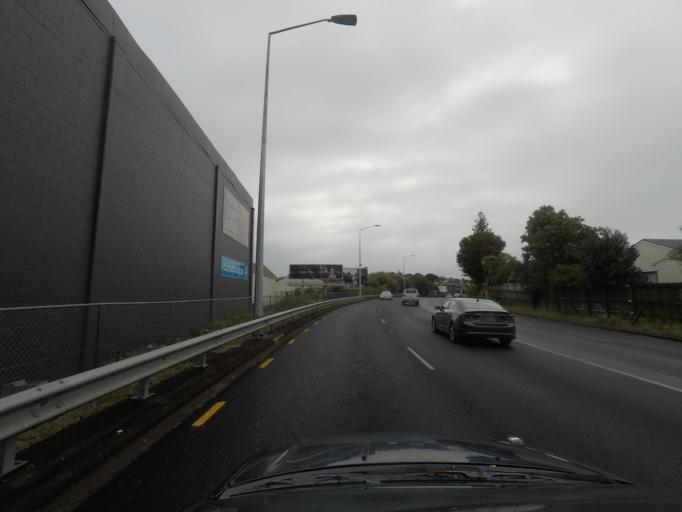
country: NZ
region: Auckland
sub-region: Auckland
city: Tamaki
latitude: -36.9011
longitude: 174.8132
